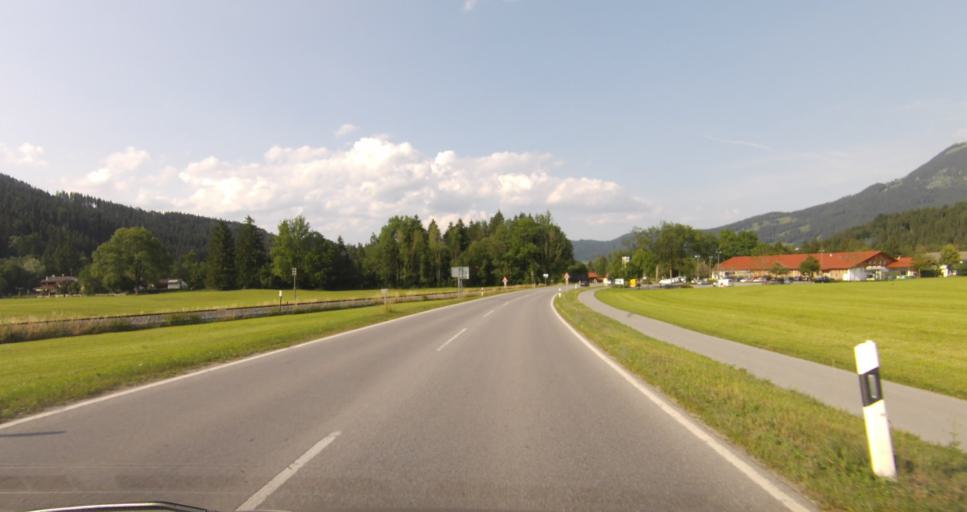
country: DE
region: Bavaria
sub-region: Upper Bavaria
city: Fischbachau
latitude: 47.7049
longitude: 11.9252
